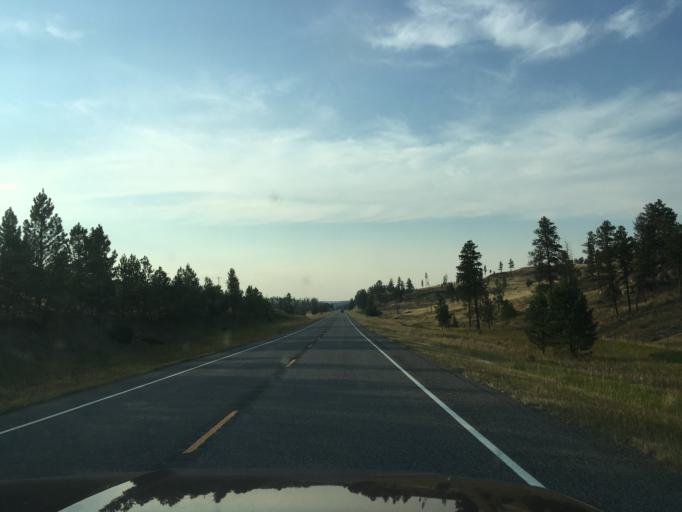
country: US
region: Montana
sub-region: Musselshell County
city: Roundup
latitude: 46.2674
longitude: -108.4695
